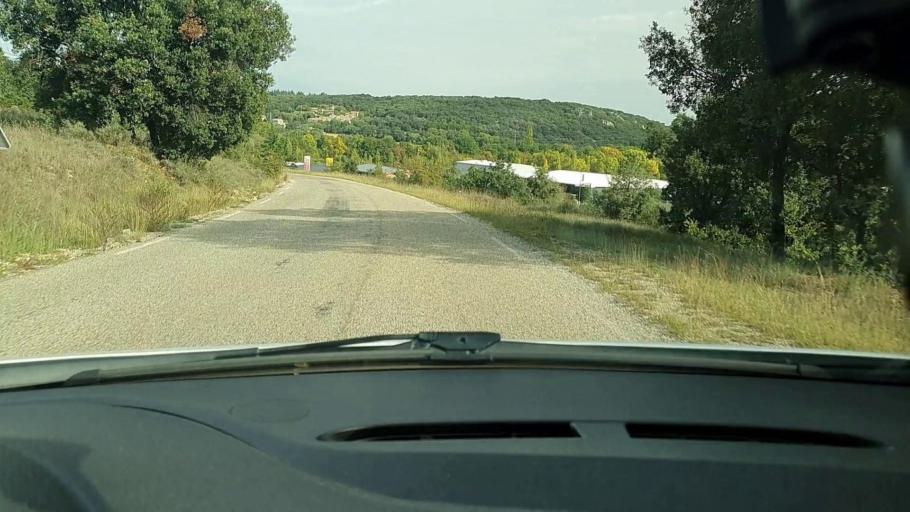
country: FR
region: Languedoc-Roussillon
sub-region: Departement du Gard
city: Saint-Quentin-la-Poterie
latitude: 44.1312
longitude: 4.4019
